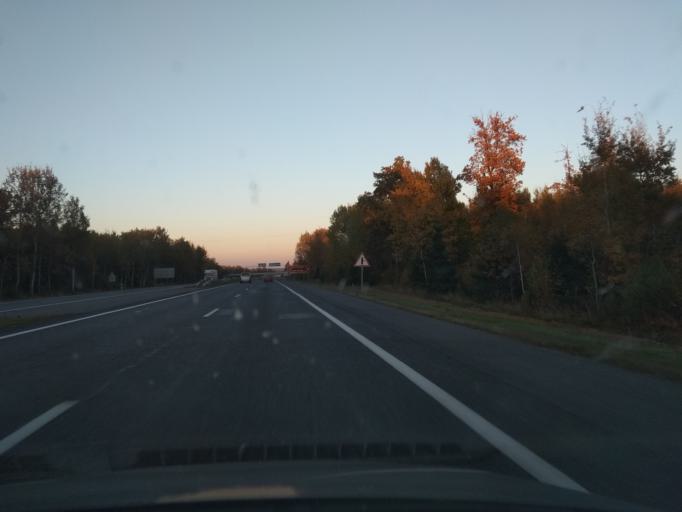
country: BY
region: Minsk
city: Haradzyeya
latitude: 53.3777
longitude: 26.5038
